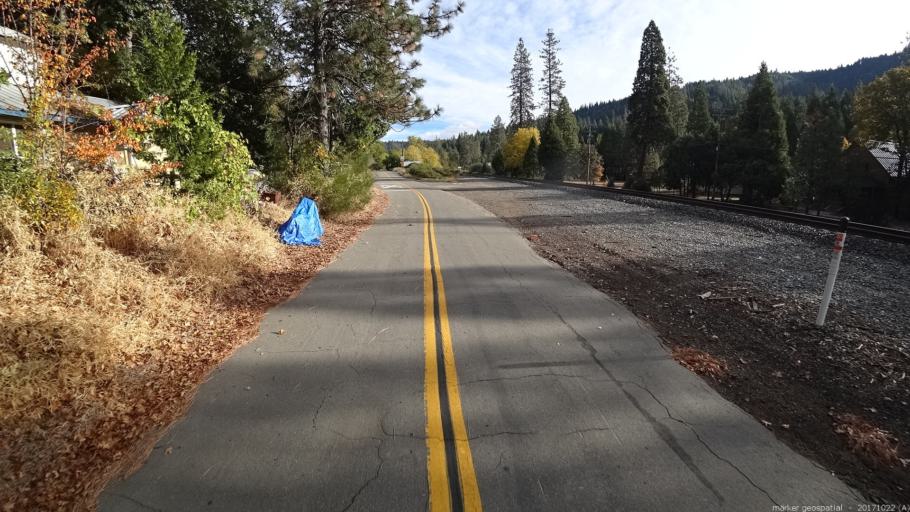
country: US
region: California
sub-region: Siskiyou County
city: Dunsmuir
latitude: 41.1389
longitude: -122.3185
